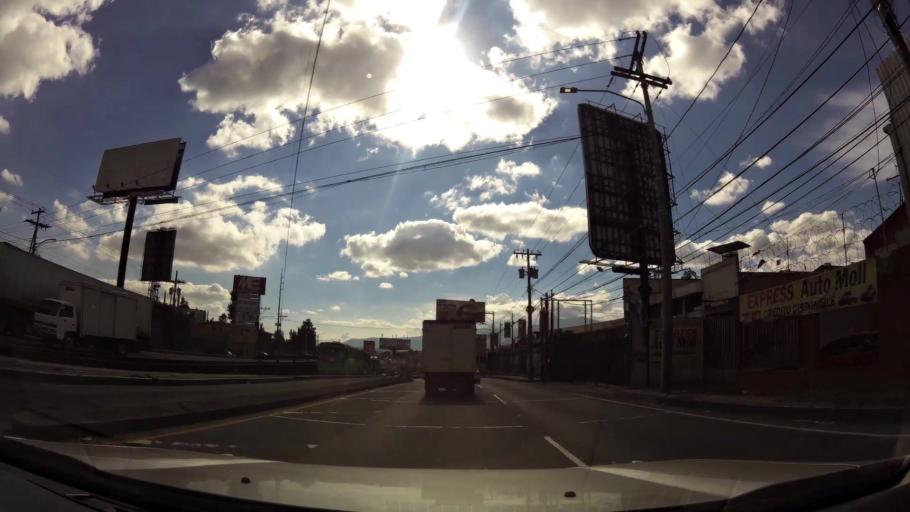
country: GT
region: Guatemala
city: Villa Nueva
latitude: 14.5762
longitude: -90.5713
